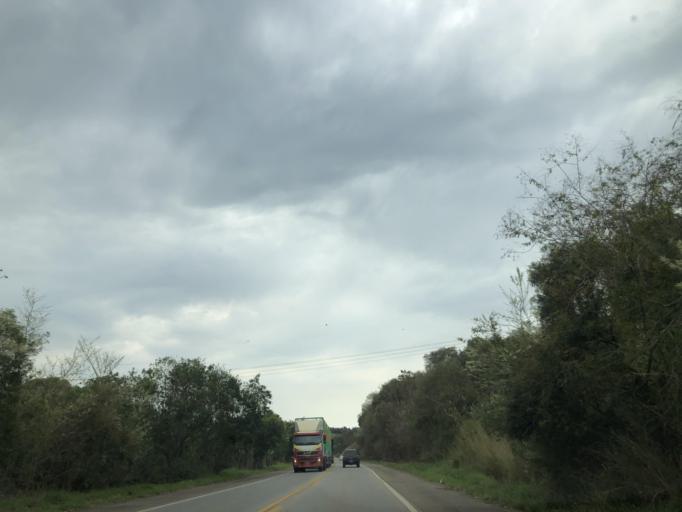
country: BR
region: Sao Paulo
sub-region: Salto De Pirapora
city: Salto de Pirapora
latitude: -23.7206
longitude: -47.6385
